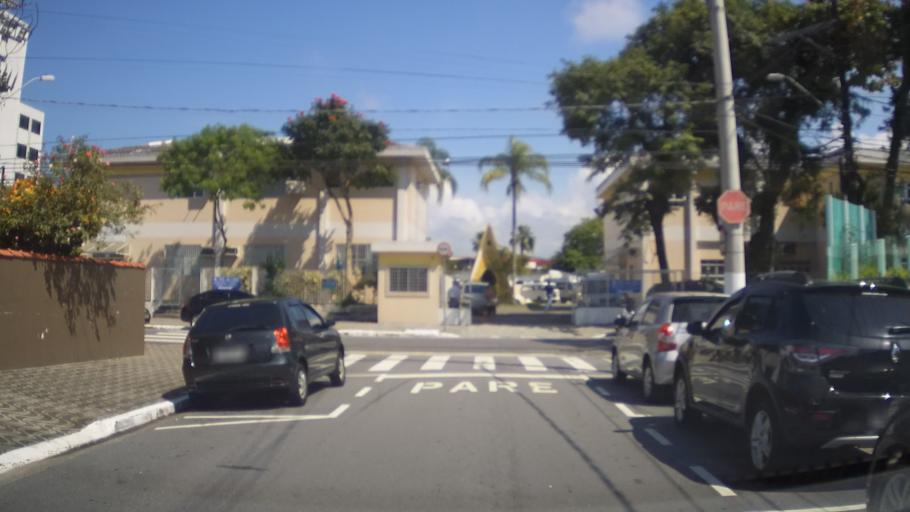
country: BR
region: Sao Paulo
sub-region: Praia Grande
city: Praia Grande
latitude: -24.0044
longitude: -46.4178
